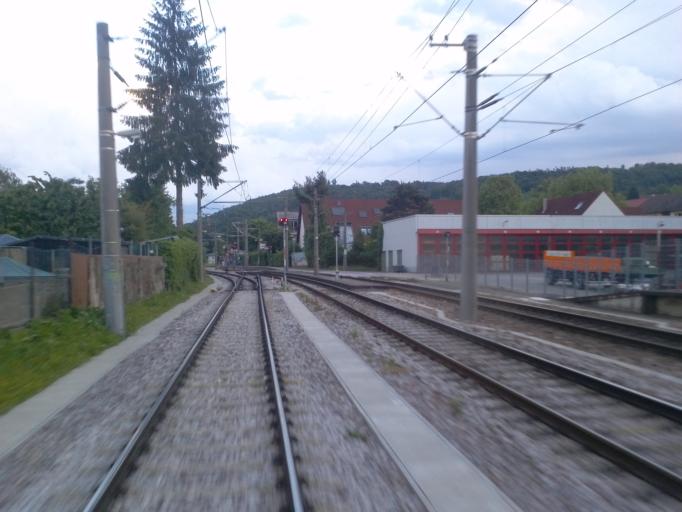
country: DE
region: Baden-Wuerttemberg
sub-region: Karlsruhe Region
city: Ettlingen
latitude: 48.9373
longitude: 8.4136
